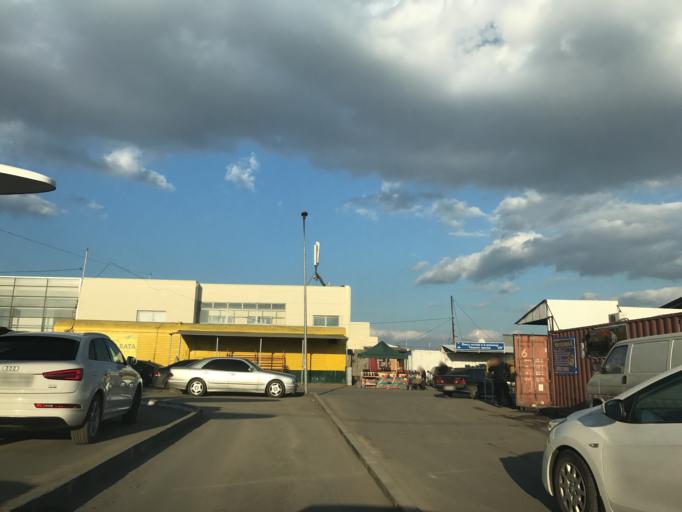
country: RU
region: Rostov
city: Aksay
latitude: 47.2737
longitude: 39.8293
